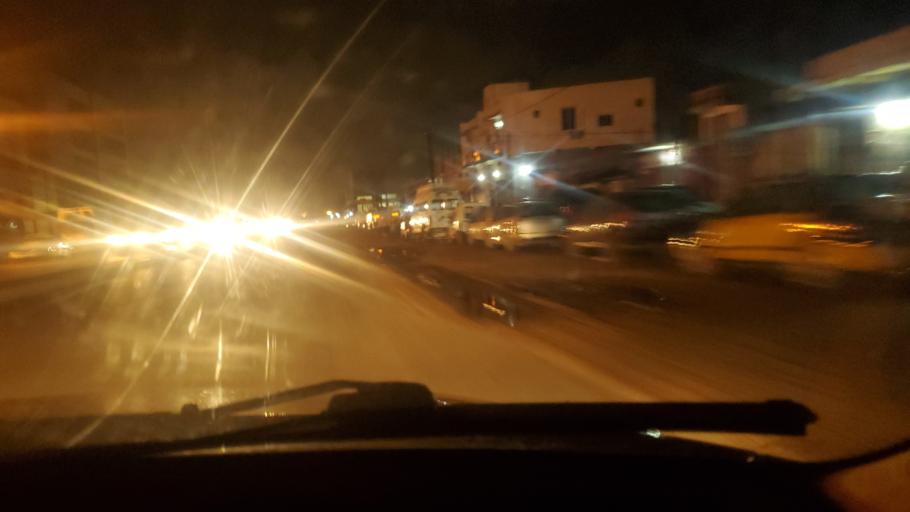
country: SN
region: Dakar
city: Pikine
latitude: 14.7447
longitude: -17.3822
